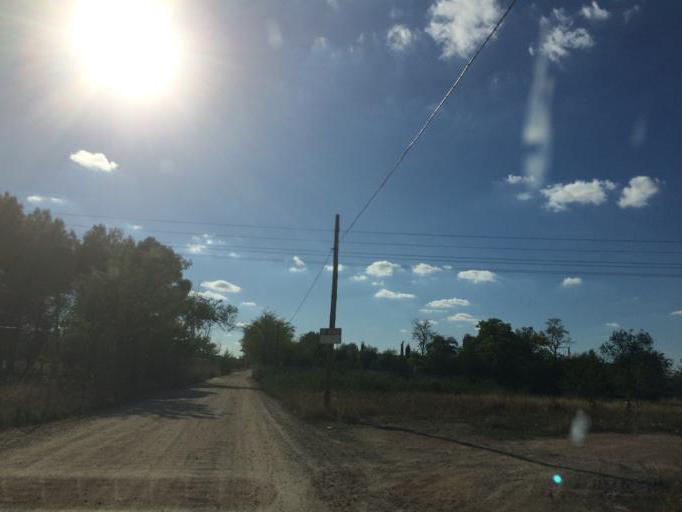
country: ES
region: Castille-La Mancha
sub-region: Provincia de Albacete
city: Albacete
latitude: 38.9931
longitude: -1.8854
